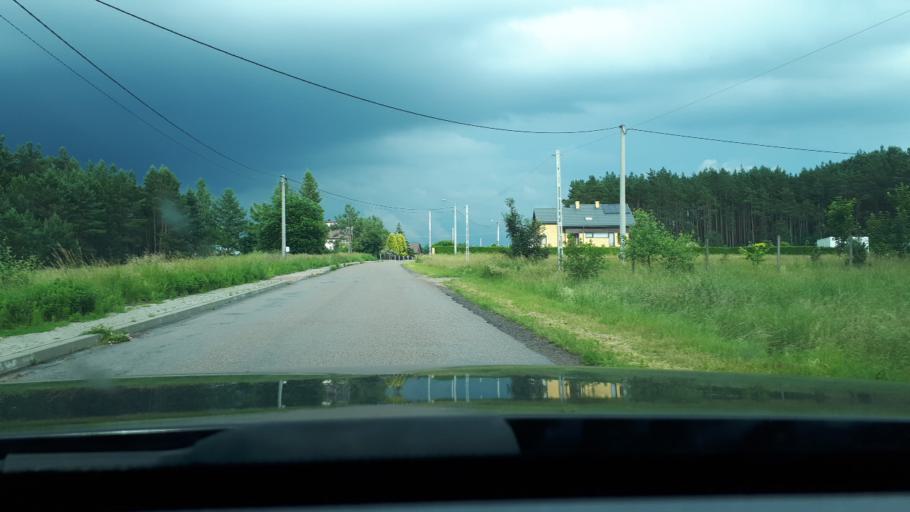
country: PL
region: Podlasie
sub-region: Powiat moniecki
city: Knyszyn
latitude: 53.2736
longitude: 22.9726
